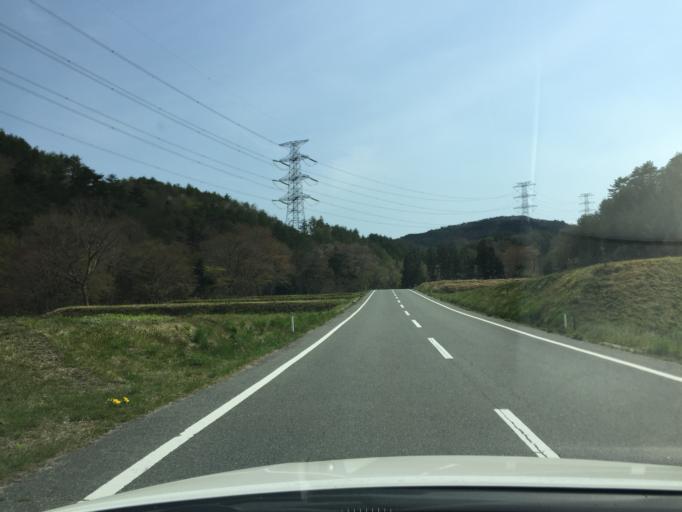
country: JP
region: Fukushima
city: Iwaki
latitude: 37.2734
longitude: 140.8371
